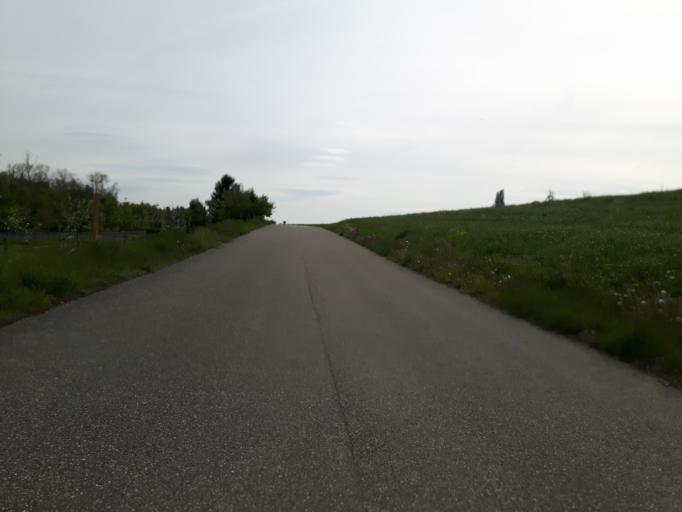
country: CH
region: Vaud
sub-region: Jura-Nord vaudois District
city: Yvonand
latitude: 46.8472
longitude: 6.7142
